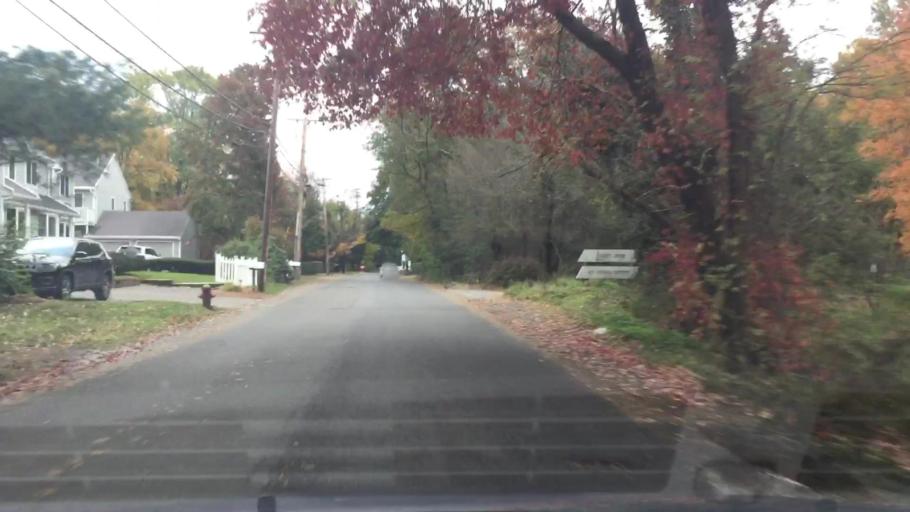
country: US
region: Massachusetts
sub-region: Essex County
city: Saugus
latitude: 42.4992
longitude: -71.0200
